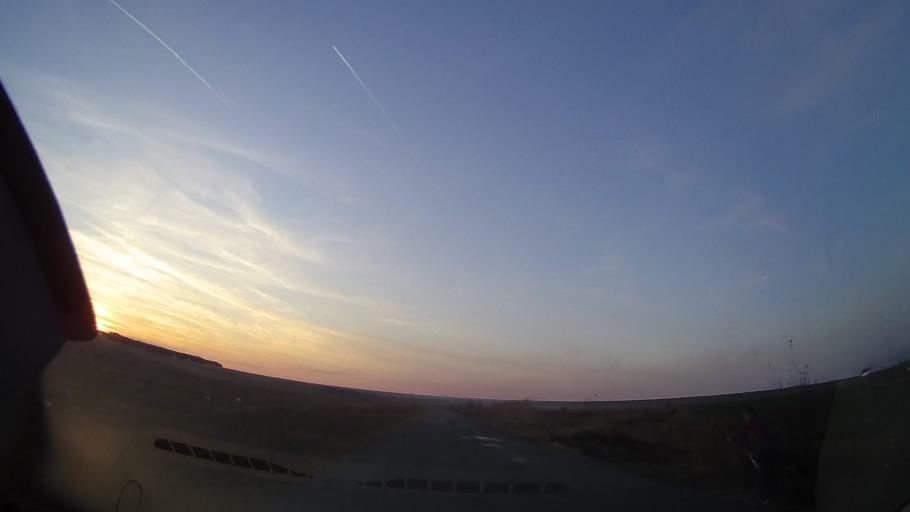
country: RO
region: Constanta
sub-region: Comuna Mereni
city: Mereni
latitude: 44.0169
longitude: 28.3051
